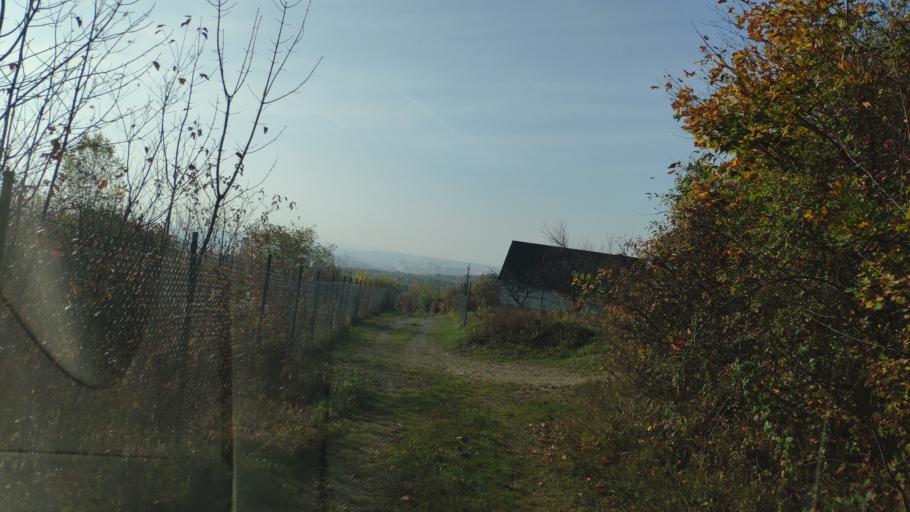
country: SK
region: Kosicky
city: Kosice
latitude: 48.7441
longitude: 21.2198
